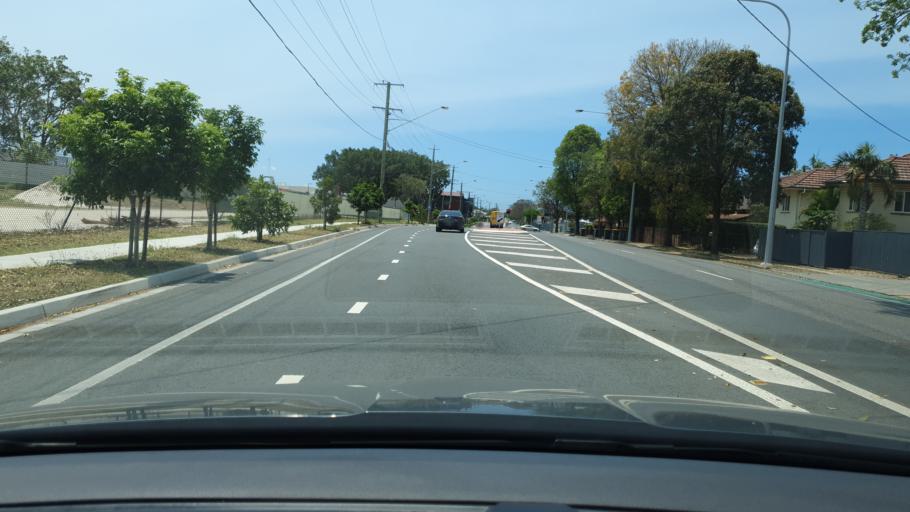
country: AU
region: Queensland
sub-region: Brisbane
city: Ascot
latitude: -27.4299
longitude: 153.0719
